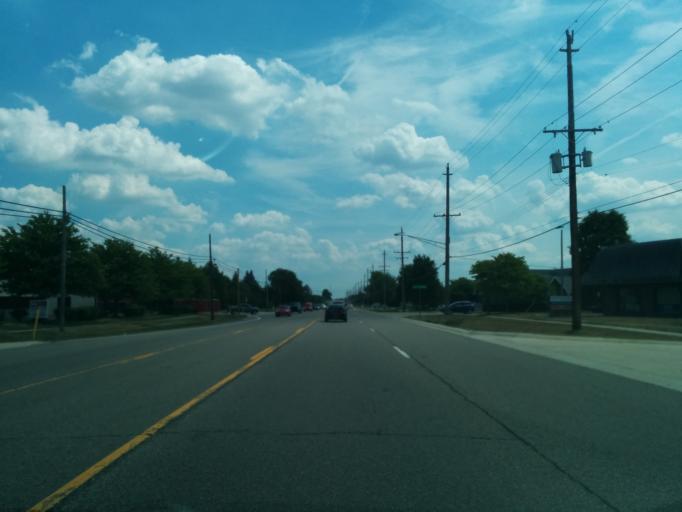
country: US
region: Michigan
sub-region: Oakland County
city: Novi
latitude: 42.4737
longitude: -83.4437
